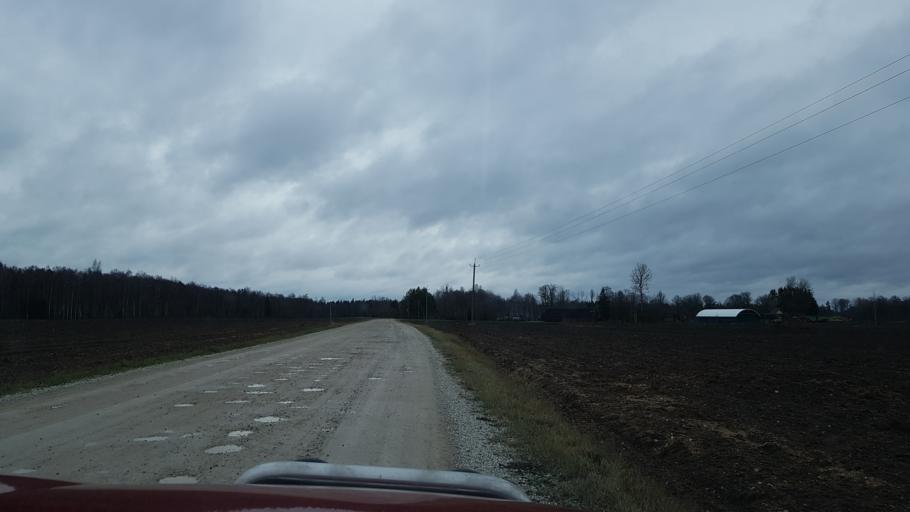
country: EE
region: Paernumaa
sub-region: Halinga vald
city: Parnu-Jaagupi
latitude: 58.5649
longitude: 24.4114
